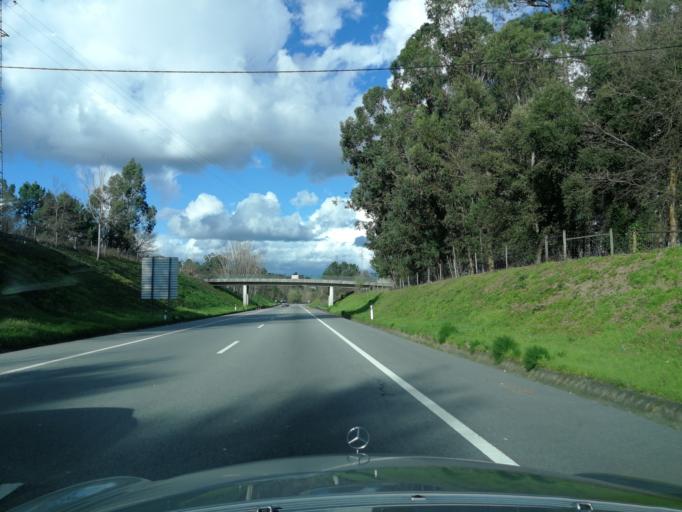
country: PT
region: Braga
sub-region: Vila Verde
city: Prado
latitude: 41.6124
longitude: -8.4545
